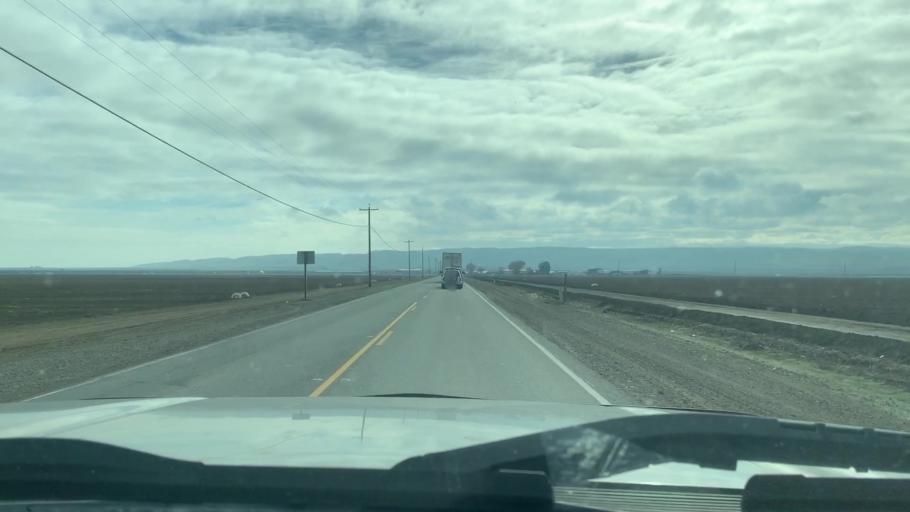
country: US
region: California
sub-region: Merced County
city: Los Banos
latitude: 36.9685
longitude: -120.8376
